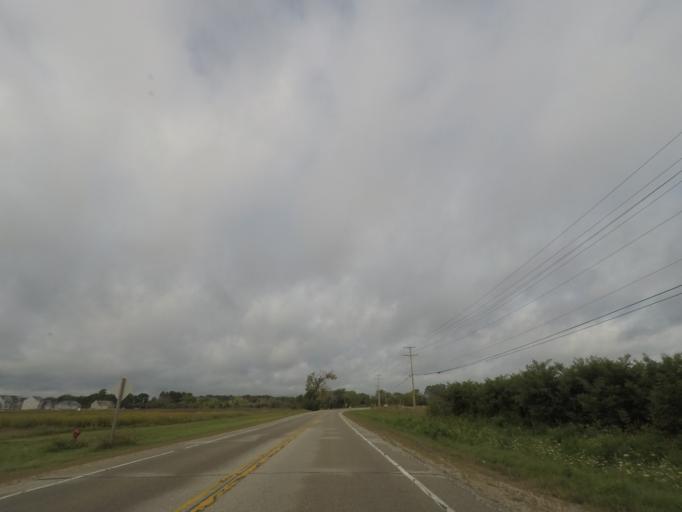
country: US
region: Wisconsin
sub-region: Waukesha County
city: Dousman
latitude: 43.0214
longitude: -88.4908
